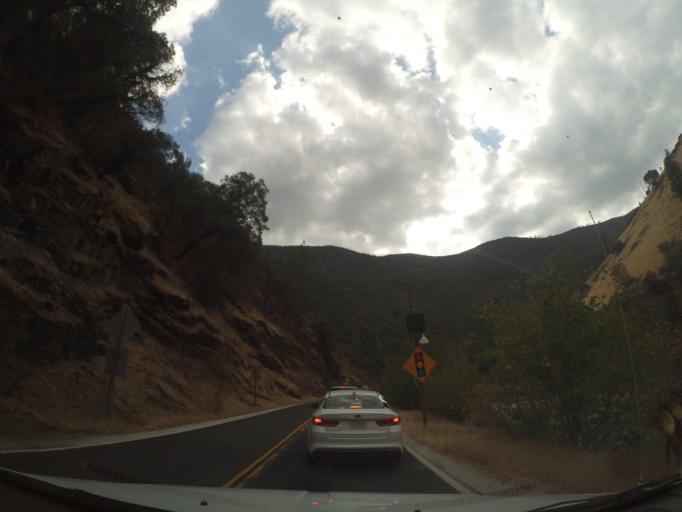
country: US
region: California
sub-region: Mariposa County
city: Midpines
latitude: 37.6561
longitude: -119.8948
